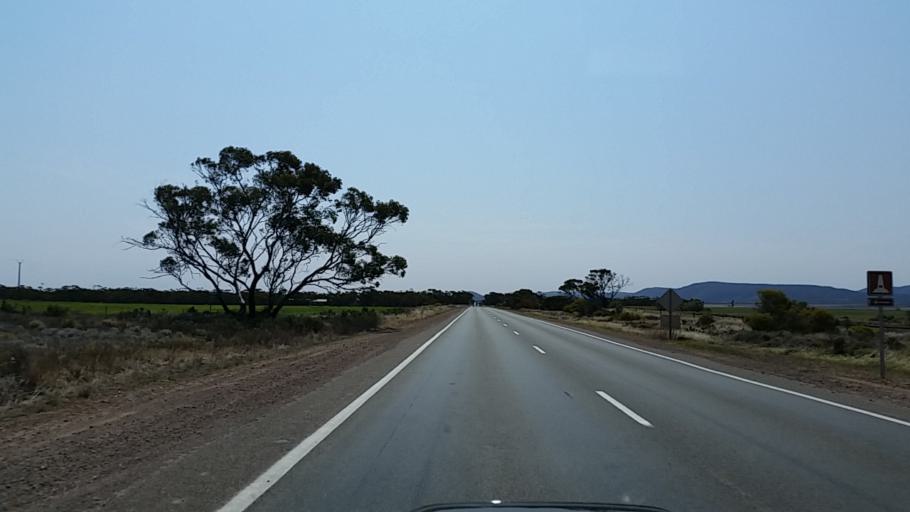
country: AU
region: South Australia
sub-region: Port Pirie City and Dists
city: Port Pirie
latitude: -32.9240
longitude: 137.9823
